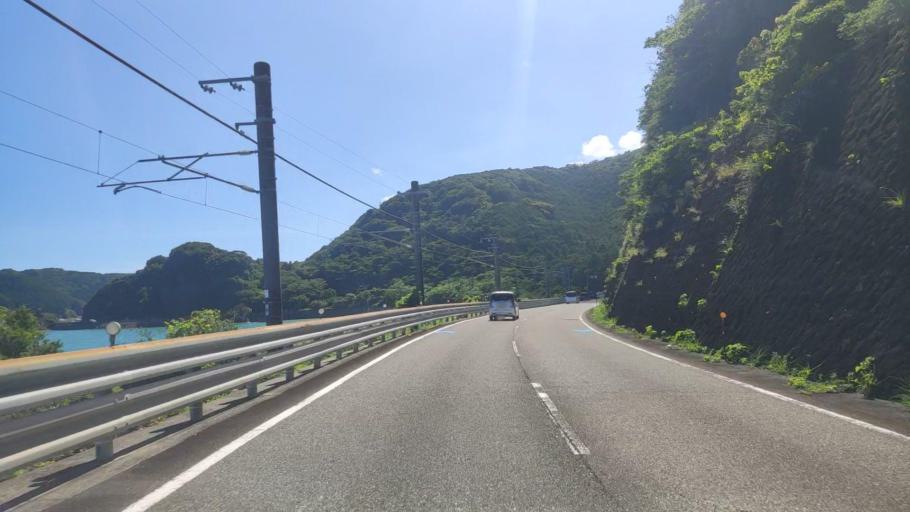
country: JP
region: Wakayama
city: Shingu
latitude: 33.5662
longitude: 135.9075
